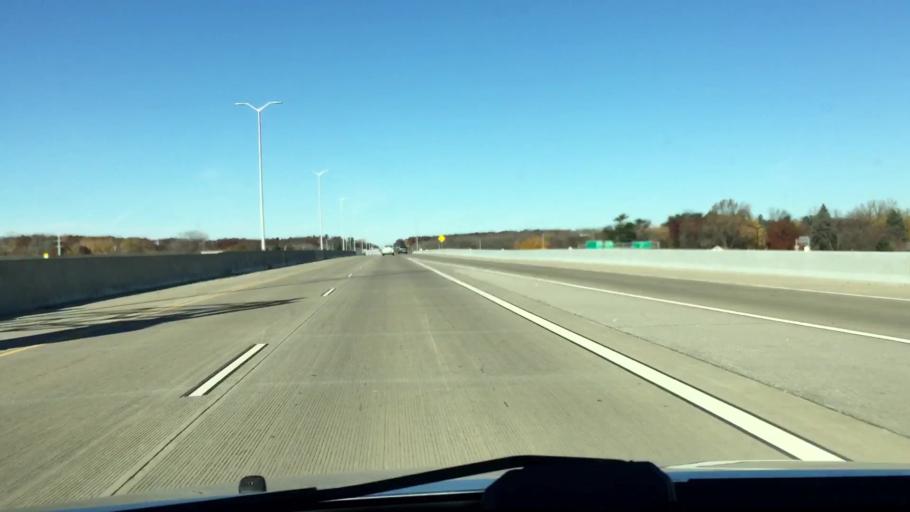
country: US
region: Wisconsin
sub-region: Brown County
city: Howard
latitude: 44.5419
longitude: -88.0850
